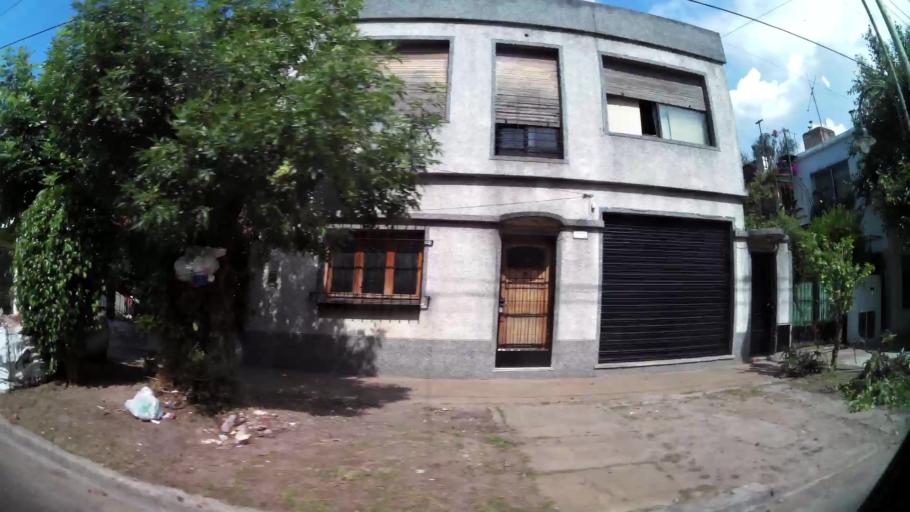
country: AR
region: Buenos Aires
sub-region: Partido de Tigre
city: Tigre
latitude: -34.4670
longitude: -58.5755
